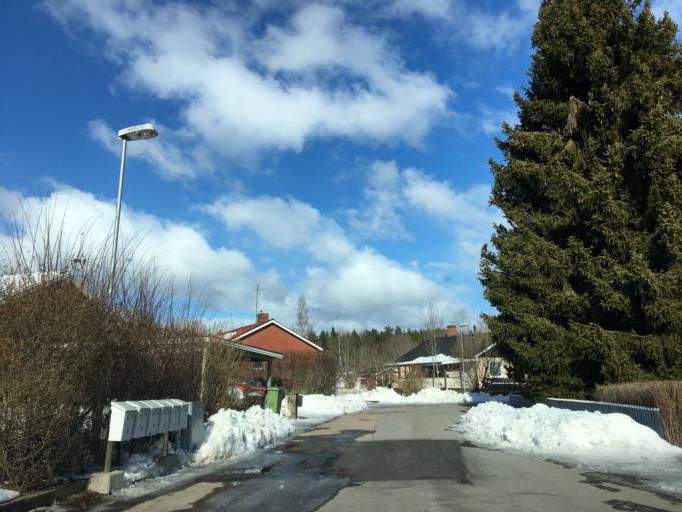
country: SE
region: Vaestmanland
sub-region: Hallstahammars Kommun
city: Kolback
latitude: 59.5717
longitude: 16.3842
